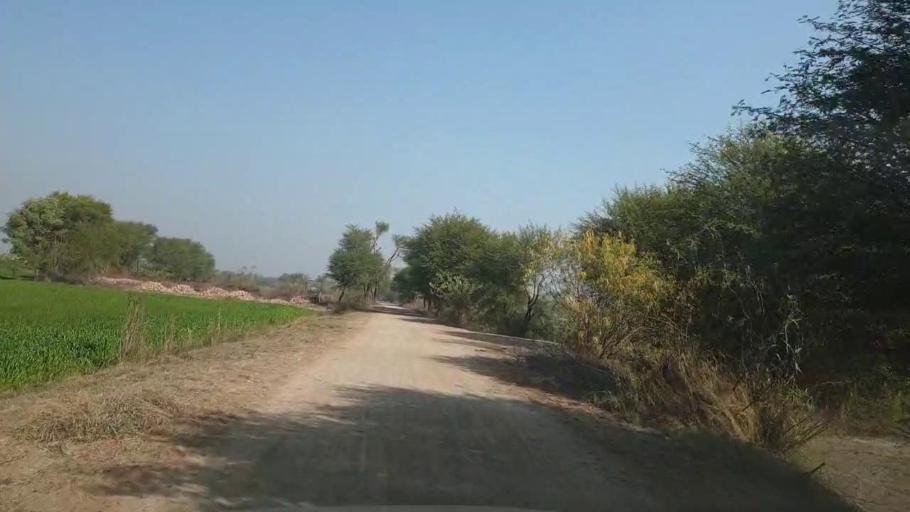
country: PK
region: Sindh
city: Matiari
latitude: 25.5495
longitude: 68.4905
